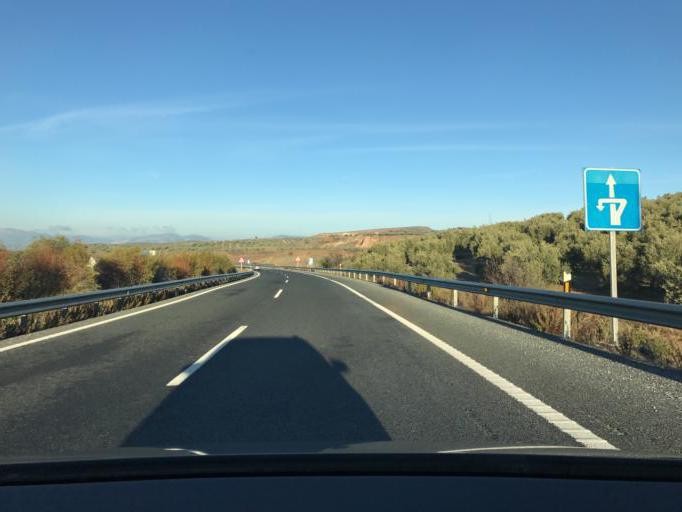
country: ES
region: Andalusia
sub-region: Provincia de Granada
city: Pulianas
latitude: 37.2375
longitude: -3.6030
